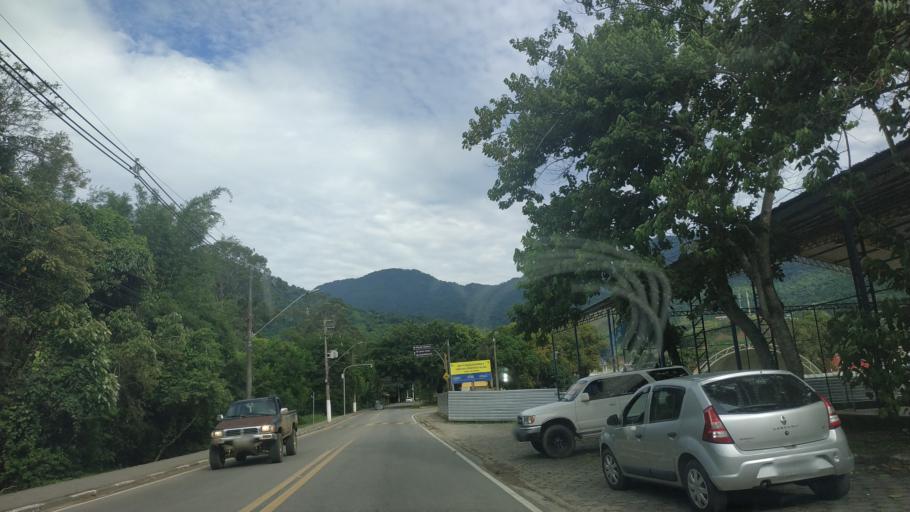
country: BR
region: Sao Paulo
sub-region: Ilhabela
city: Ilhabela
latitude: -23.8194
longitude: -45.3626
